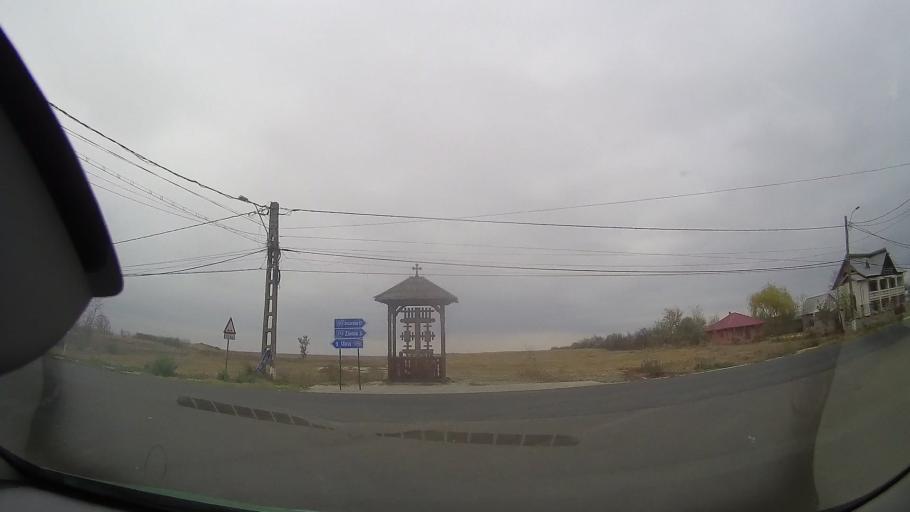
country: RO
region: Braila
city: Dudesti
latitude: 44.9430
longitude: 27.4245
